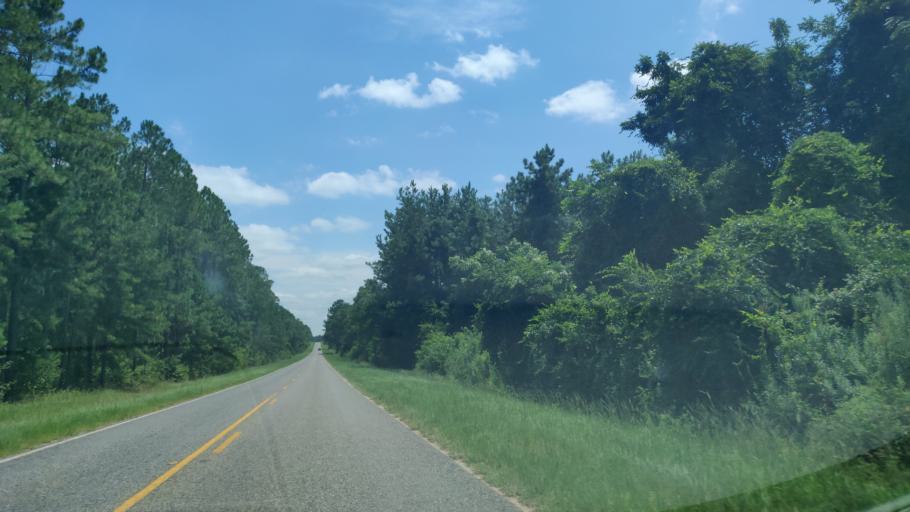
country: US
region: Georgia
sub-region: Tift County
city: Omega
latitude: 31.4585
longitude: -83.6375
